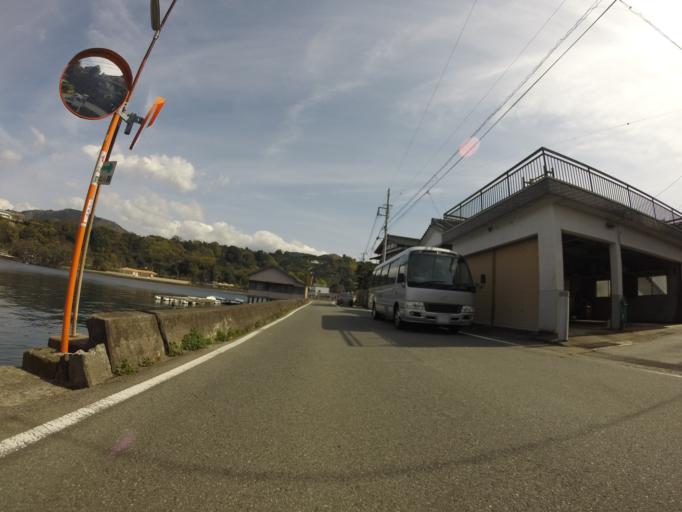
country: JP
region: Shizuoka
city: Numazu
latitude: 35.0217
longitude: 138.8773
